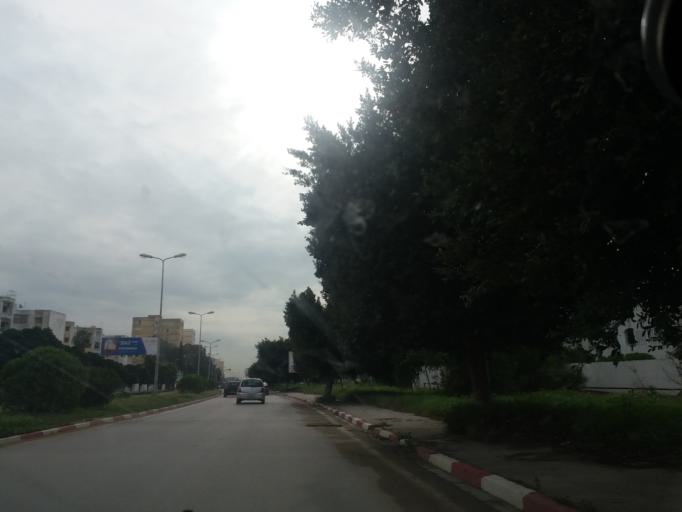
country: TN
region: Tunis
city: Tunis
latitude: 36.8481
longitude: 10.1582
